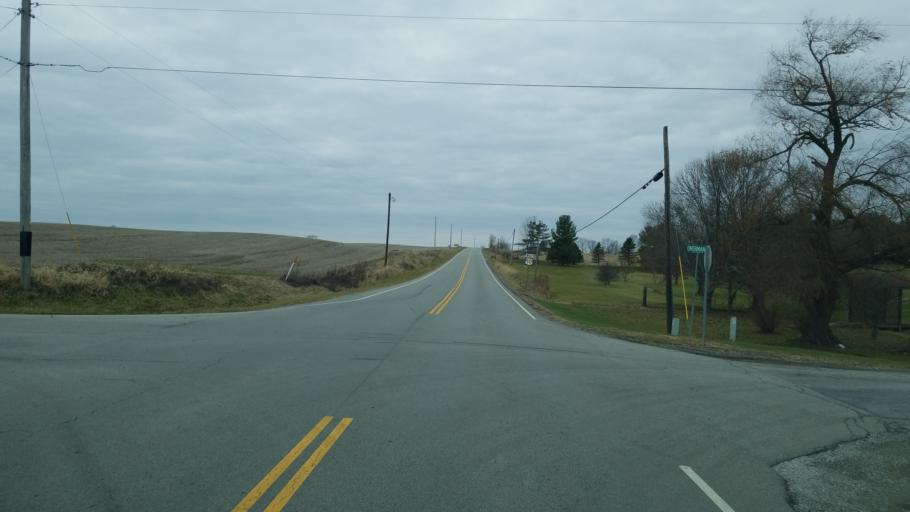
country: US
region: Ohio
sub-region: Highland County
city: Hillsboro
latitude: 39.2165
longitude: -83.4857
